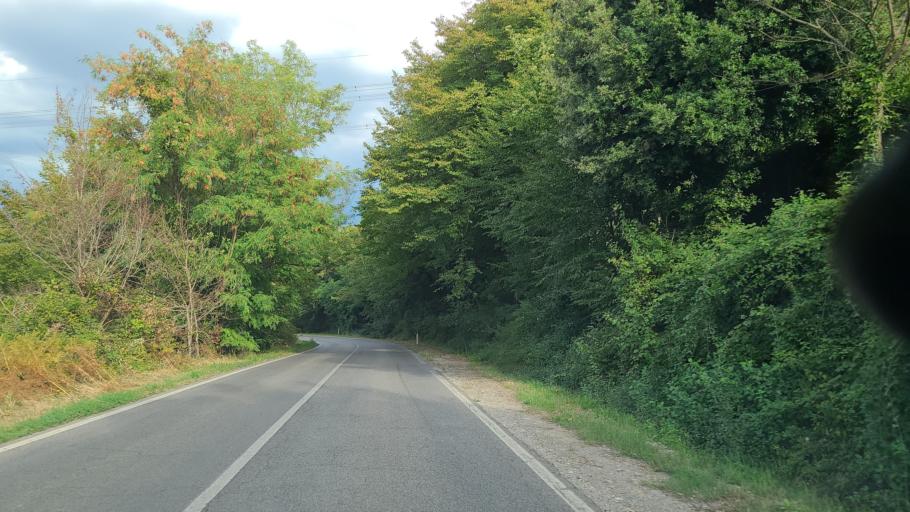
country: IT
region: Tuscany
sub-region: Provincia di Siena
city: San Gimignano
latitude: 43.4866
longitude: 10.9939
